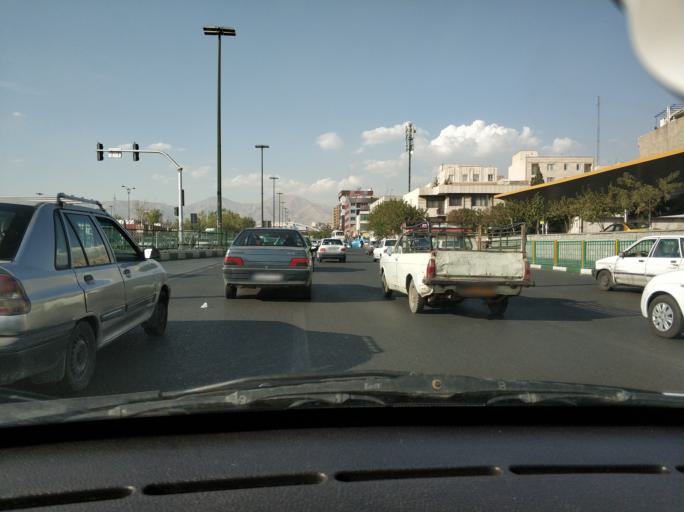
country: IR
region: Tehran
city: Tehran
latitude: 35.7027
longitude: 51.3377
